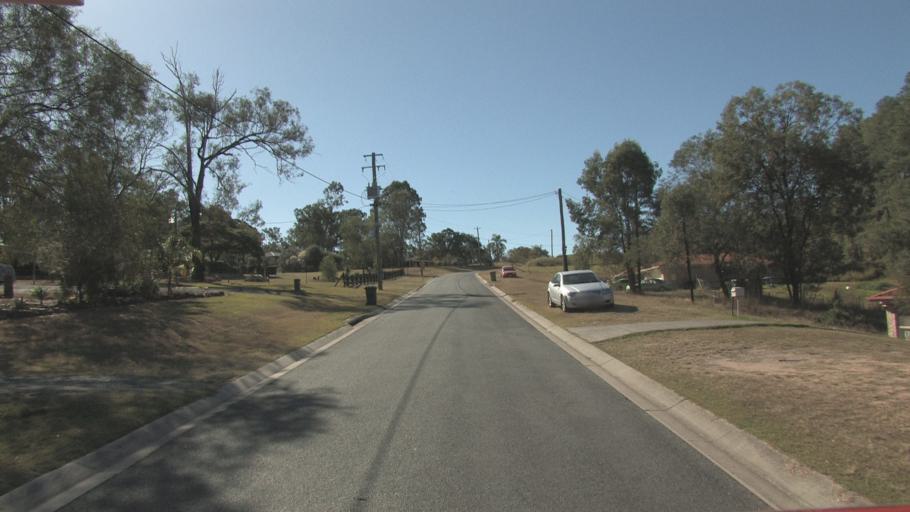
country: AU
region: Queensland
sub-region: Logan
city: Cedar Vale
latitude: -27.8556
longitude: 153.0120
